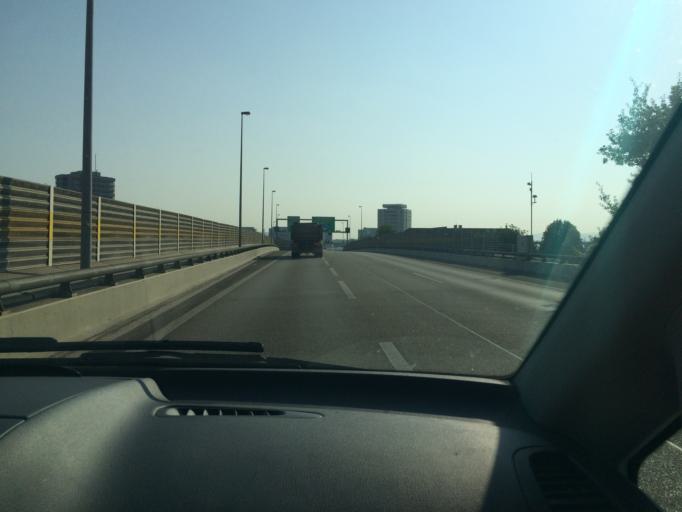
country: CH
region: Basel-Landschaft
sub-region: Bezirk Arlesheim
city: Birsfelden
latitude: 47.5458
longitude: 7.6085
